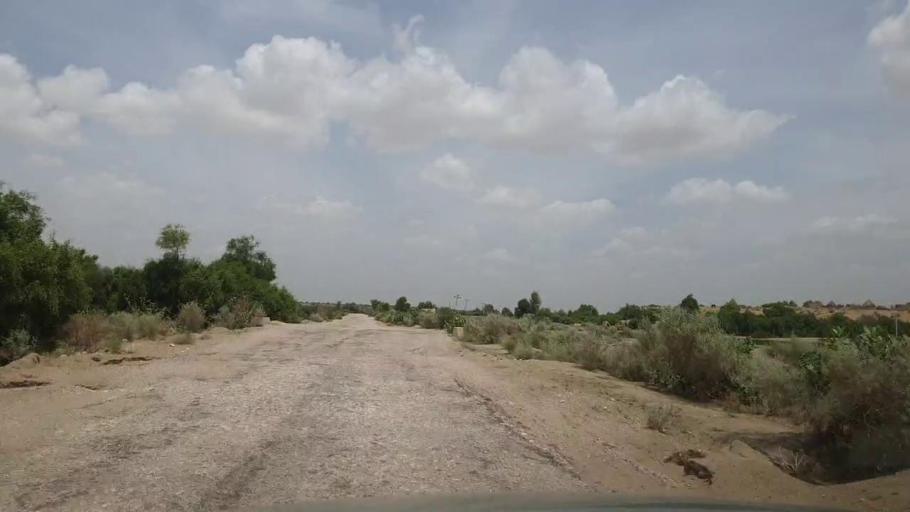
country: PK
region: Sindh
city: Kot Diji
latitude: 27.2034
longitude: 69.1394
